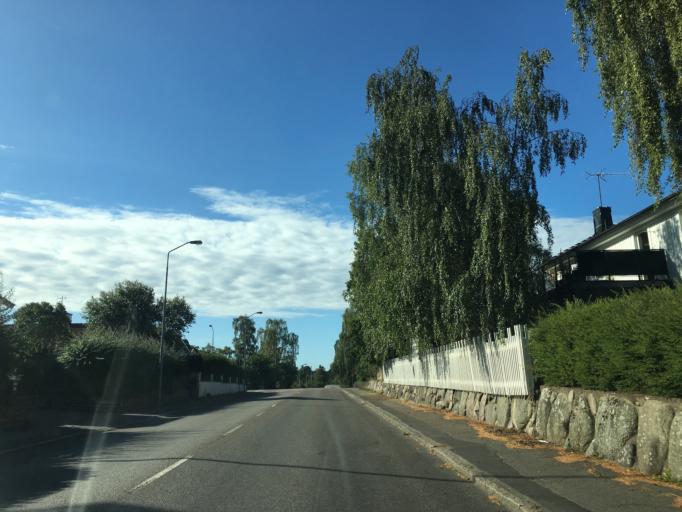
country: SE
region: Kalmar
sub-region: Kalmar Kommun
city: Kalmar
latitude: 56.6911
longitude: 16.3558
